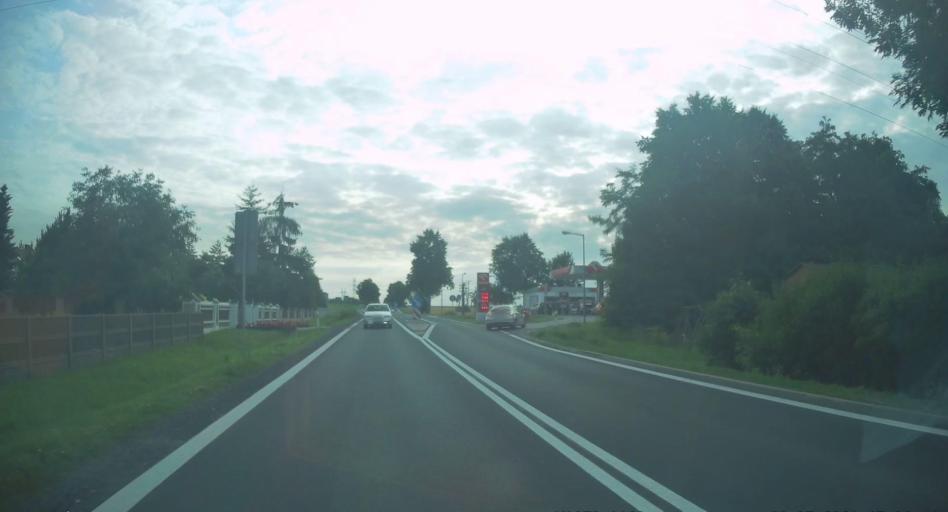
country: PL
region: Silesian Voivodeship
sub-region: Powiat czestochowski
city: Klomnice
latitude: 50.9173
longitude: 19.3358
